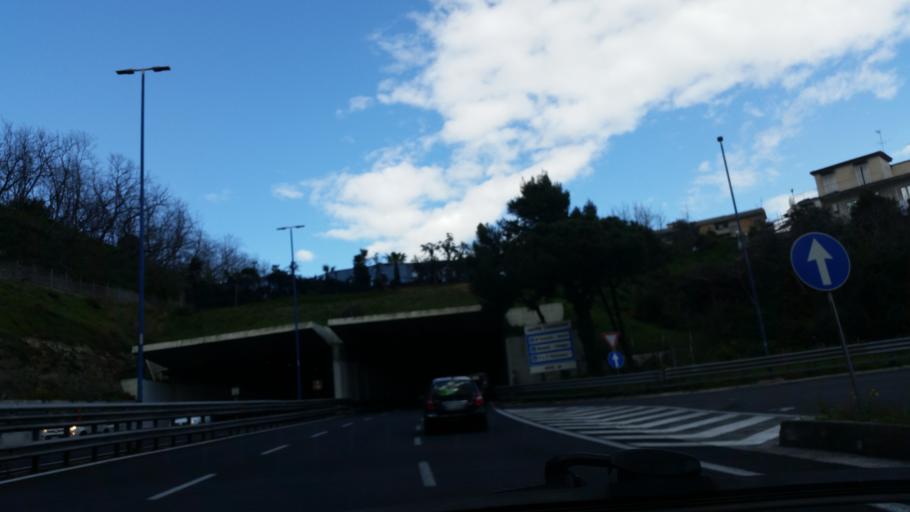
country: IT
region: Campania
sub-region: Provincia di Napoli
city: Napoli
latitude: 40.8515
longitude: 14.2154
